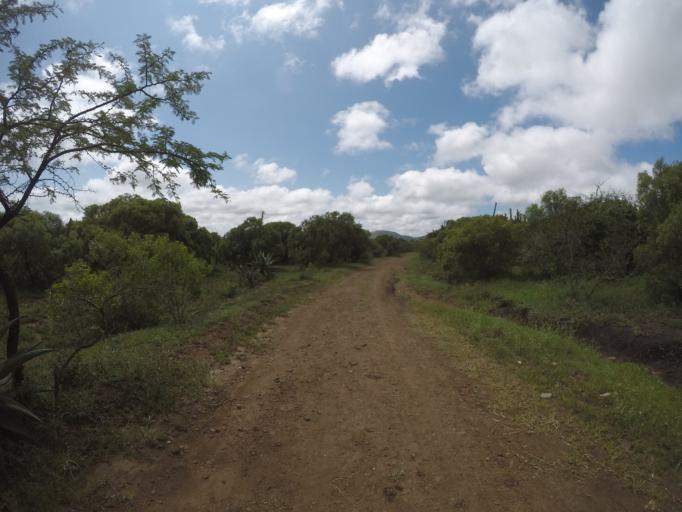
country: ZA
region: KwaZulu-Natal
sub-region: uThungulu District Municipality
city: Empangeni
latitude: -28.5726
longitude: 31.8310
